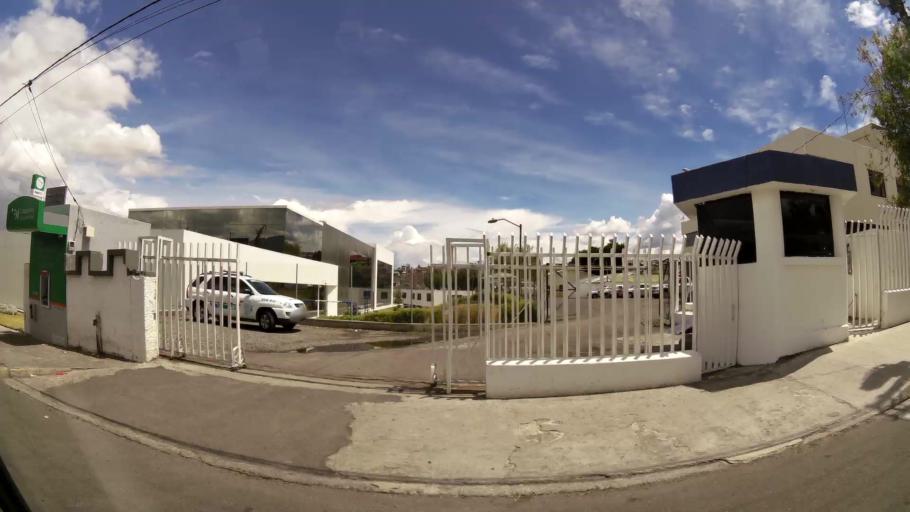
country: EC
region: Tungurahua
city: Ambato
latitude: -1.2533
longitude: -78.6345
